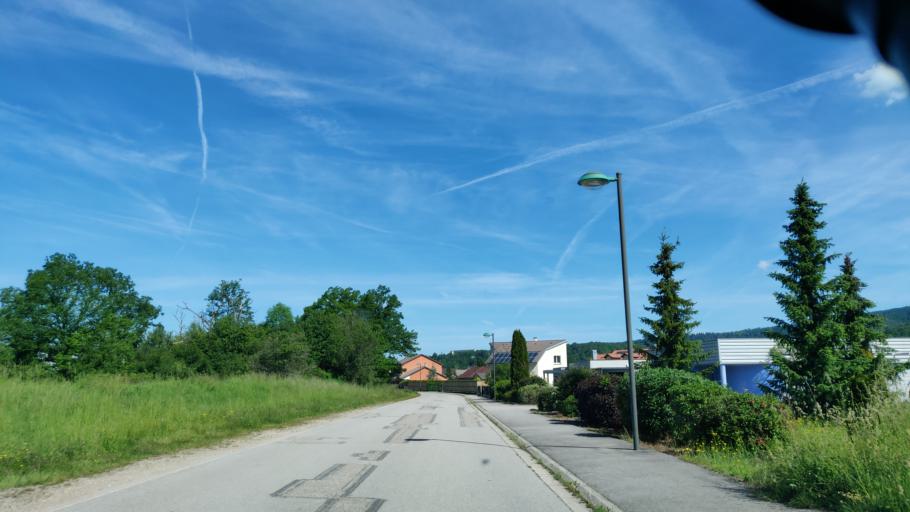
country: FR
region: Lorraine
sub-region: Departement des Vosges
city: Sainte-Marguerite
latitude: 48.2744
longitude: 6.9775
